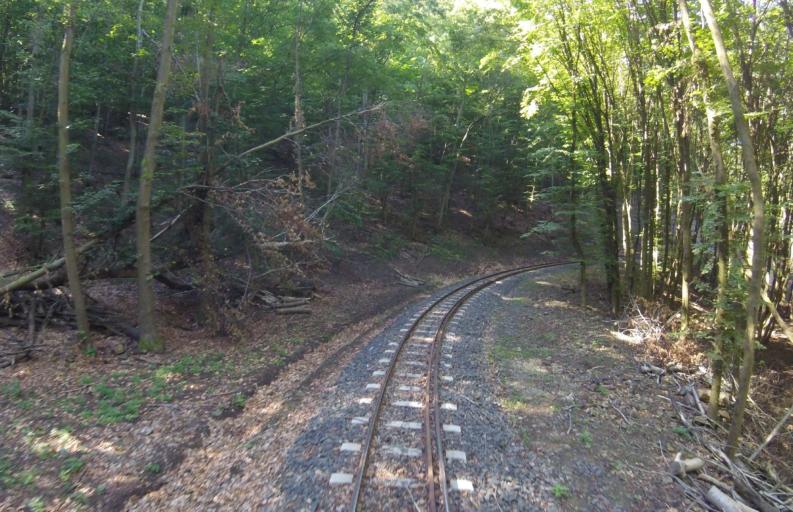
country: HU
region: Pest
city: Szob
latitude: 47.8855
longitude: 18.8669
